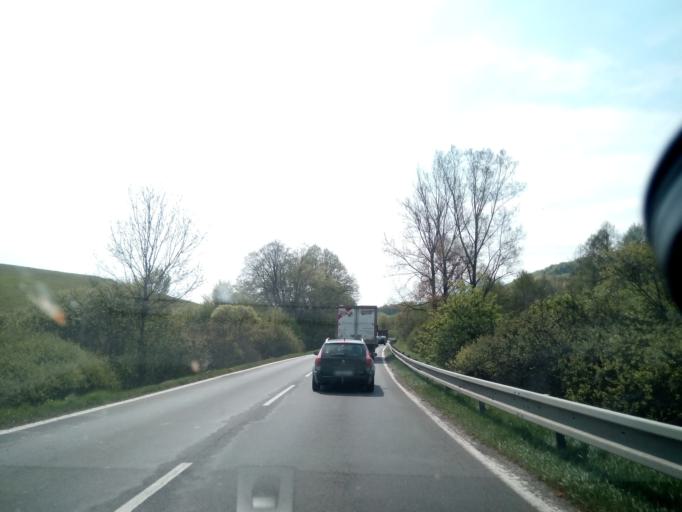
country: SK
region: Presovsky
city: Giraltovce
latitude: 49.0465
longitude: 21.4396
